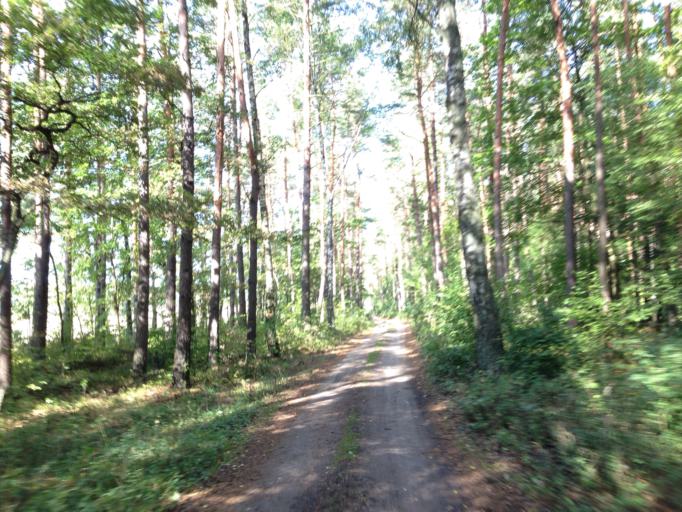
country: PL
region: Warmian-Masurian Voivodeship
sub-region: Powiat dzialdowski
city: Lidzbark
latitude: 53.2224
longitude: 19.7498
